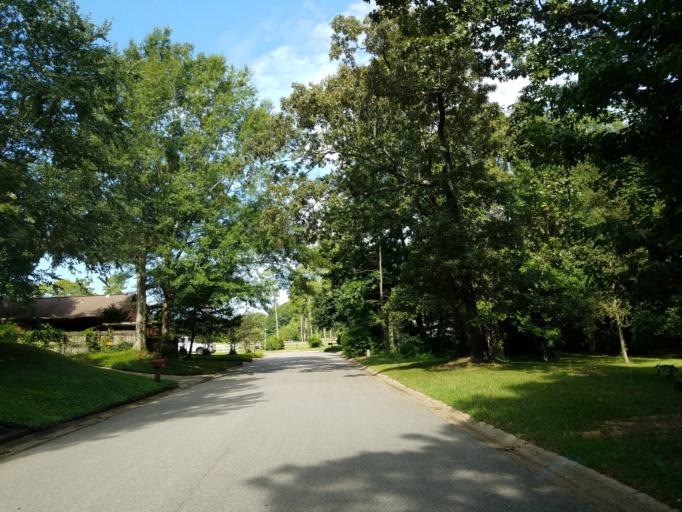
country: US
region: Mississippi
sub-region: Lamar County
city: West Hattiesburg
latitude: 31.3166
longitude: -89.3445
